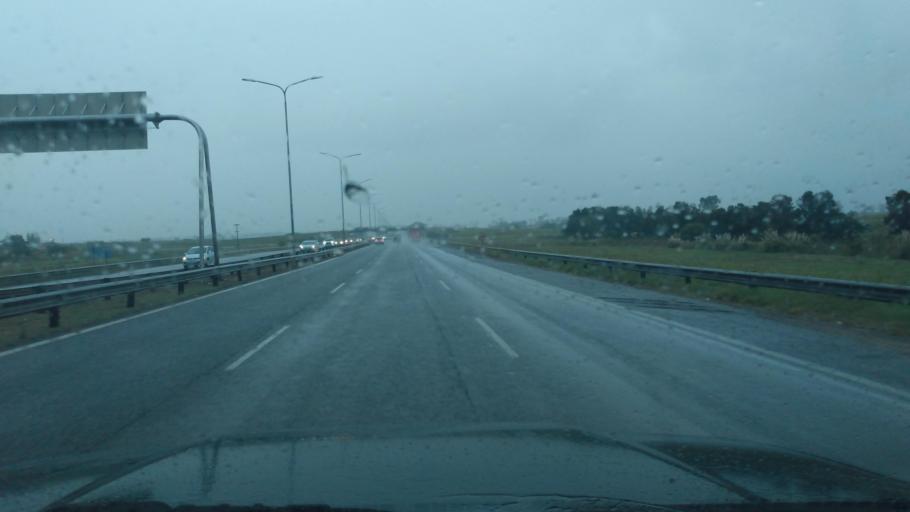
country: AR
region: Buenos Aires
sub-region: Partido de Tigre
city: Tigre
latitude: -34.5129
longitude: -58.5905
